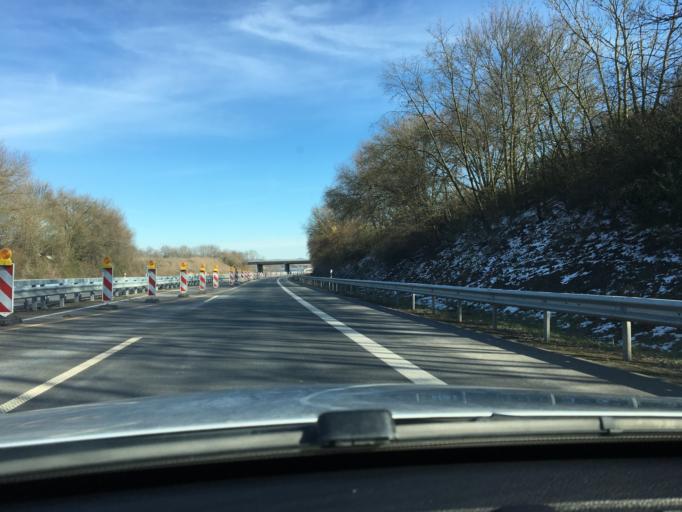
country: DE
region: Rheinland-Pfalz
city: Worms
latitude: 49.6223
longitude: 8.3299
